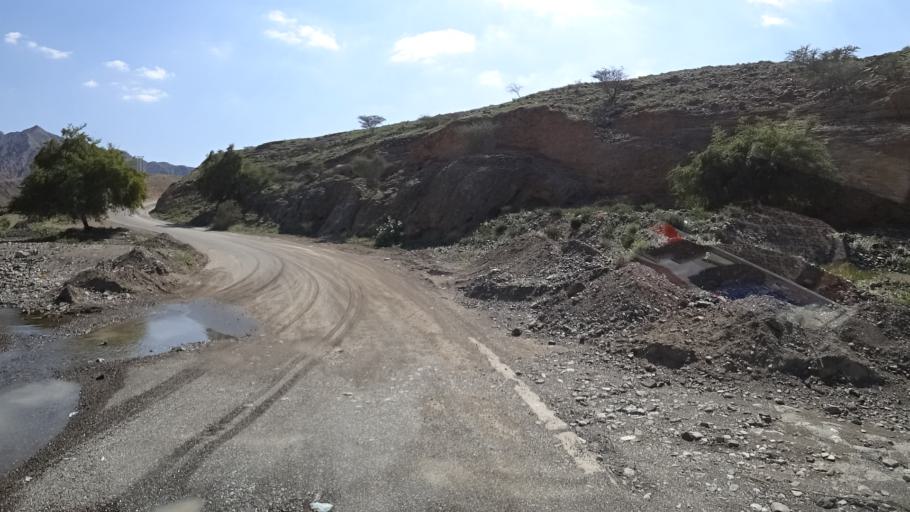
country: OM
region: Al Batinah
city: Al Khaburah
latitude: 23.6652
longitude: 56.9264
